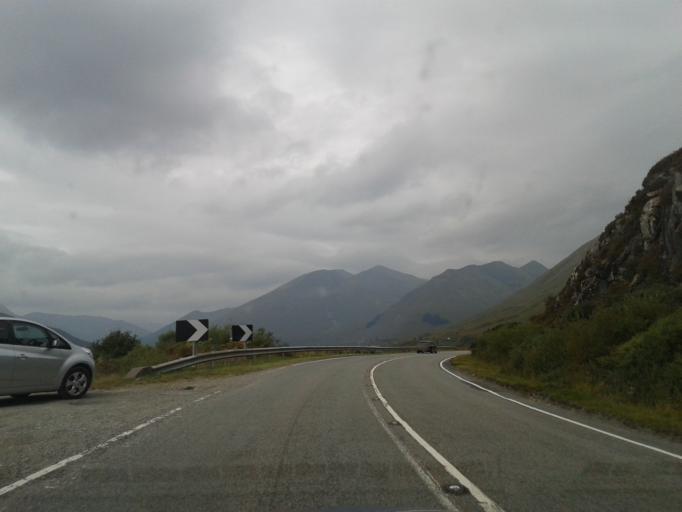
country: GB
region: Scotland
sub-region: Highland
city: Spean Bridge
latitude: 57.1486
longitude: -5.1178
